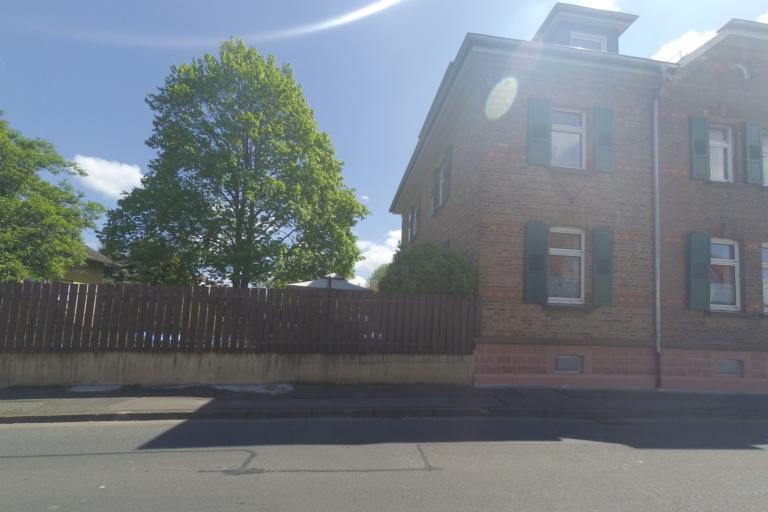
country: DE
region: Hesse
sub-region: Regierungsbezirk Darmstadt
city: Karben
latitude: 50.2403
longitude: 8.7730
